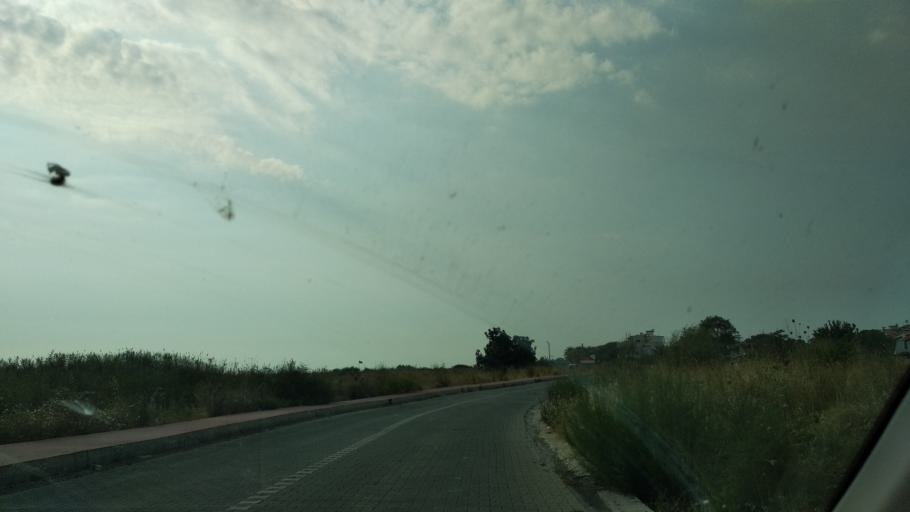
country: TR
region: Izmir
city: Dikili
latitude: 39.1054
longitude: 26.8733
